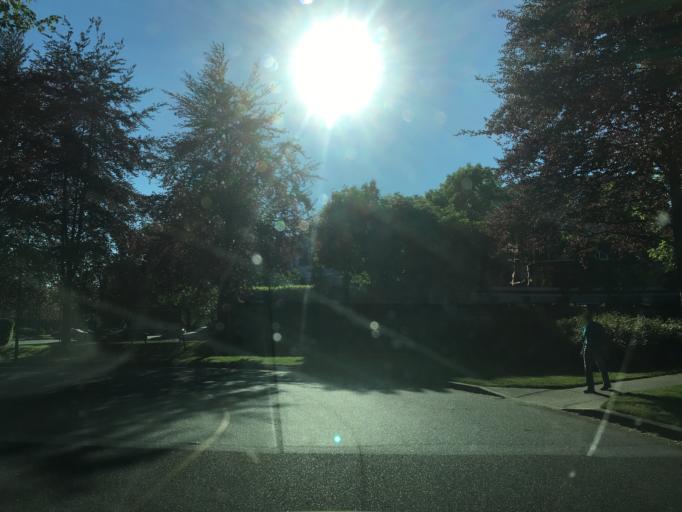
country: CA
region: British Columbia
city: Richmond
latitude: 49.1762
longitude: -123.0714
